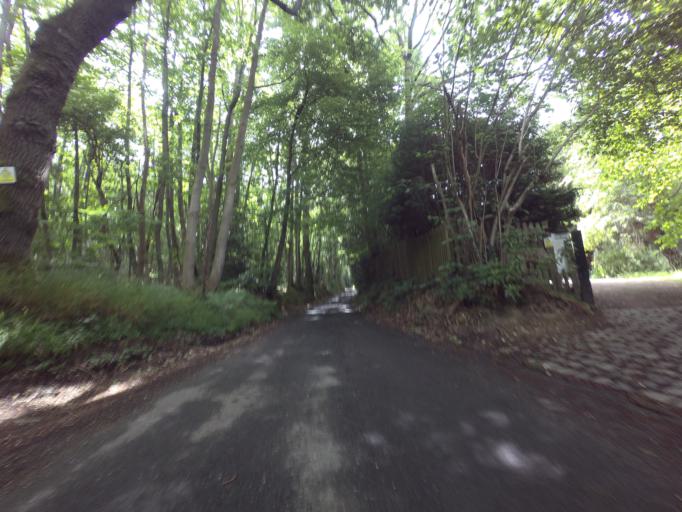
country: GB
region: England
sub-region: Kent
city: Halstead
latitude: 51.3449
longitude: 0.1453
